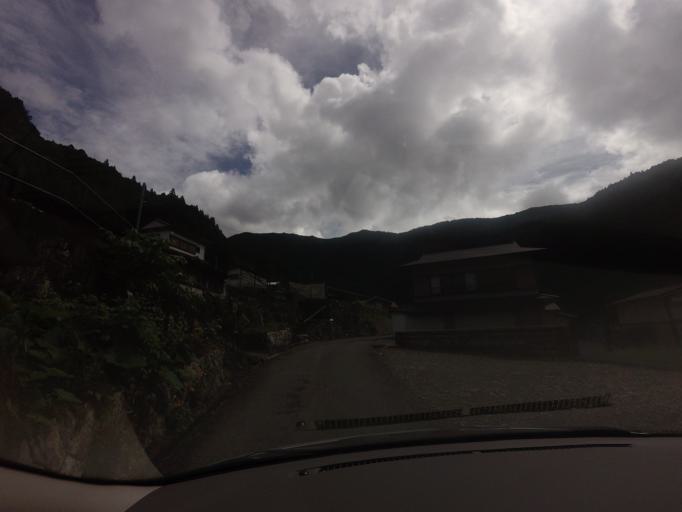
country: JP
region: Wakayama
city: Shingu
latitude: 33.9625
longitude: 135.8682
